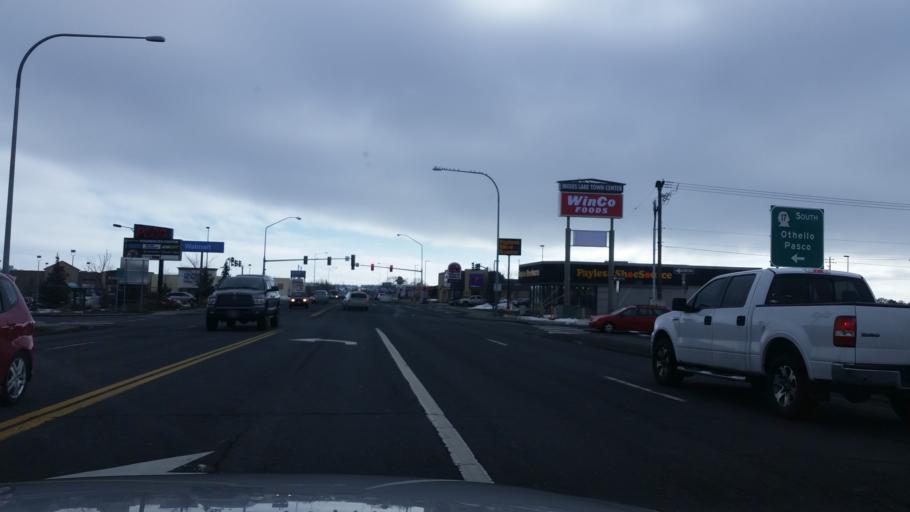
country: US
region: Washington
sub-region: Grant County
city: Moses Lake
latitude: 47.1431
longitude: -119.2784
